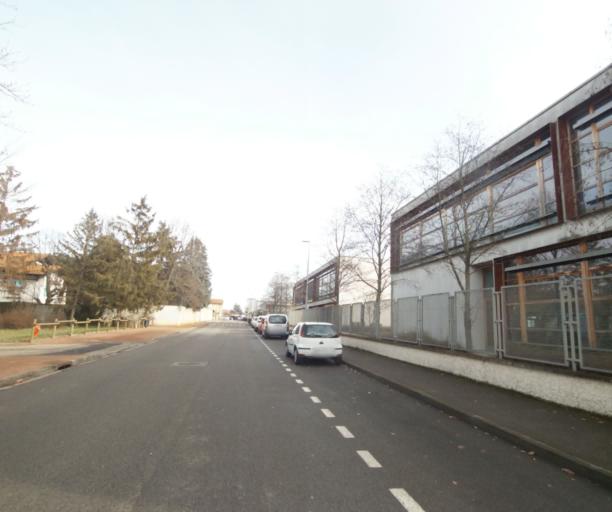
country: FR
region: Rhone-Alpes
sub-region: Departement de la Loire
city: Riorges
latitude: 46.0279
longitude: 4.0503
